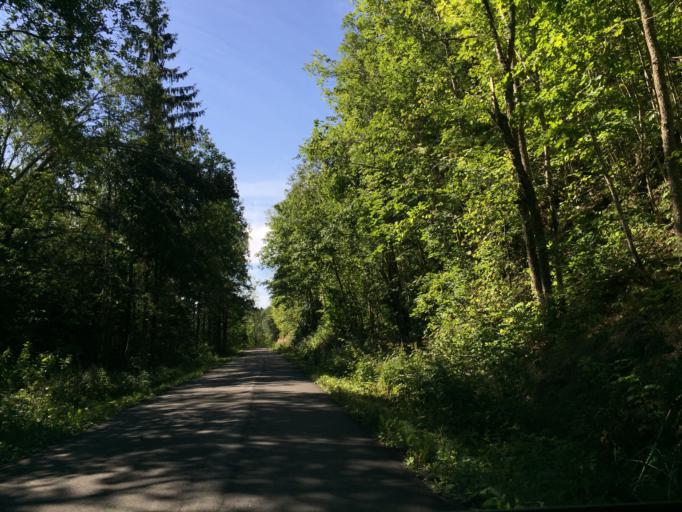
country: NO
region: Vestfold
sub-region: Hof
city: Hof
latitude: 59.4773
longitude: 10.1480
